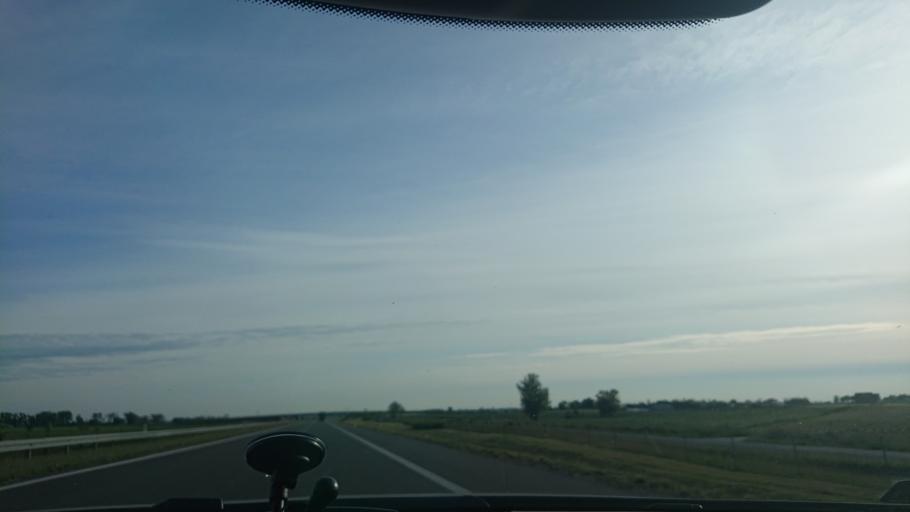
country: PL
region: Greater Poland Voivodeship
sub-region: Powiat gnieznienski
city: Gniezno
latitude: 52.5435
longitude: 17.5292
